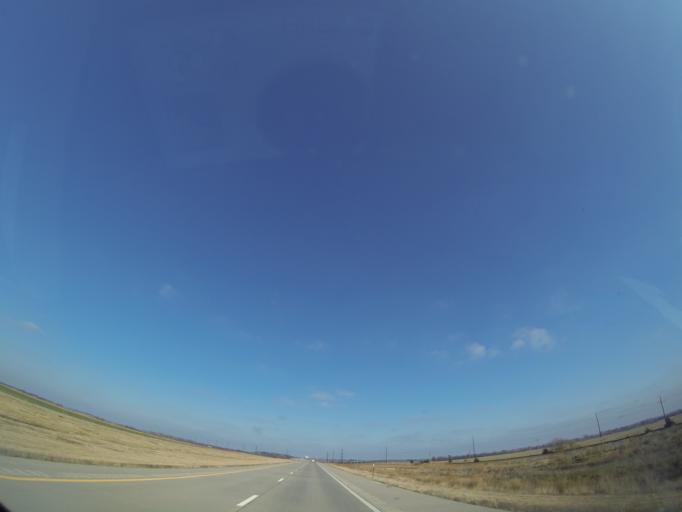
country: US
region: Kansas
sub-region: McPherson County
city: Inman
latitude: 38.1922
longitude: -97.8088
